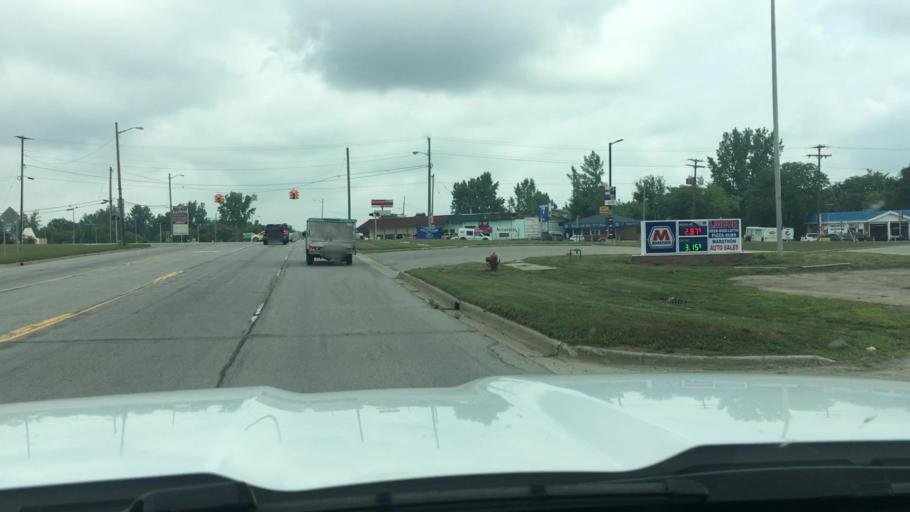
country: US
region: Michigan
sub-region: Lapeer County
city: Imlay City
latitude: 43.0295
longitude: -83.0714
